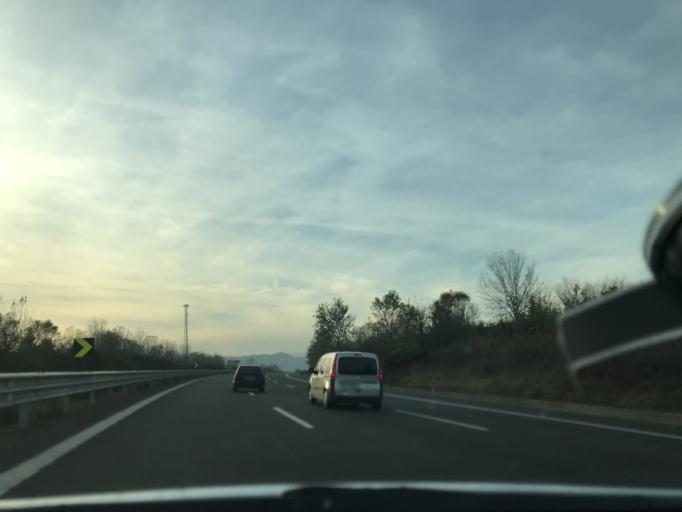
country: TR
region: Duzce
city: Gumusova
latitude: 40.8393
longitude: 30.9874
